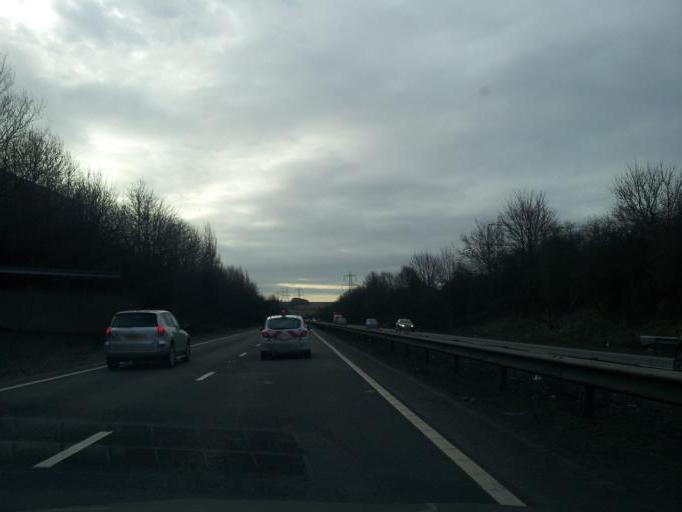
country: GB
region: England
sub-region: Lincolnshire
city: Barrowby
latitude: 52.9064
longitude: -0.6733
